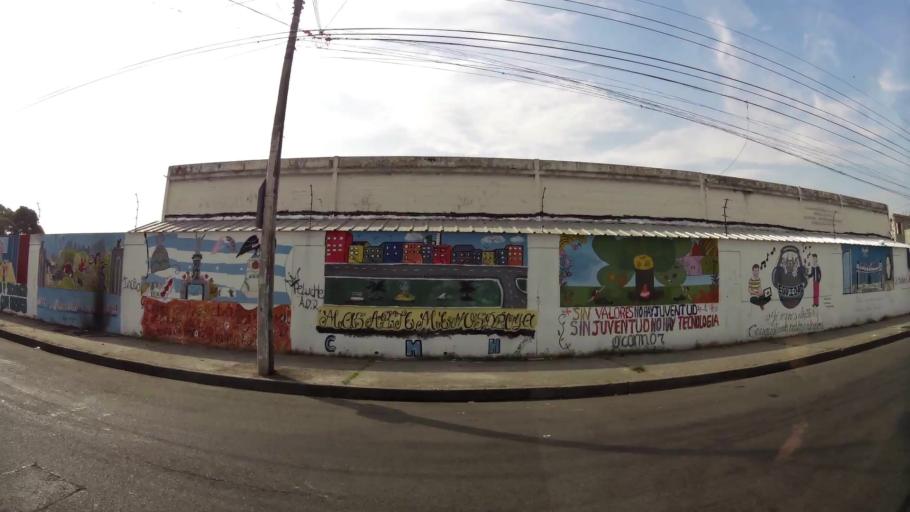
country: EC
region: Guayas
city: Guayaquil
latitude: -2.2140
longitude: -79.9047
